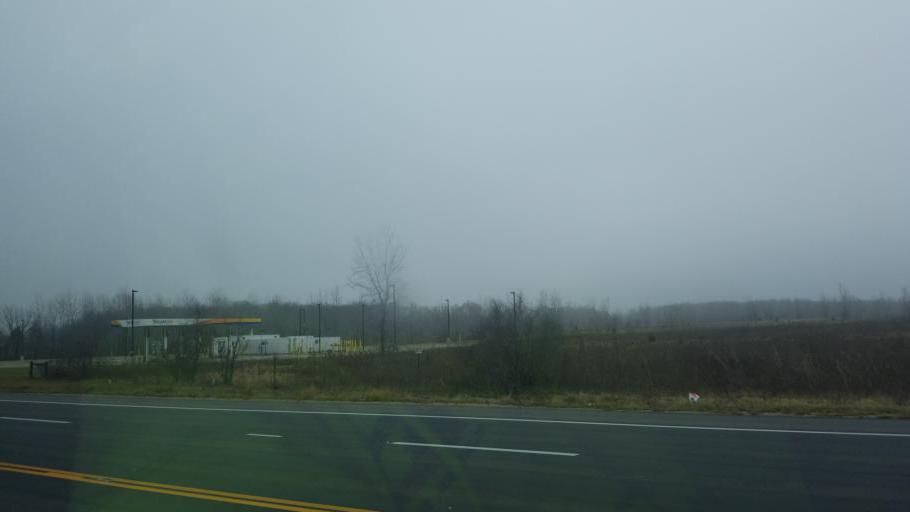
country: US
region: Ohio
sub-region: Champaign County
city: North Lewisburg
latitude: 40.2769
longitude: -83.5330
